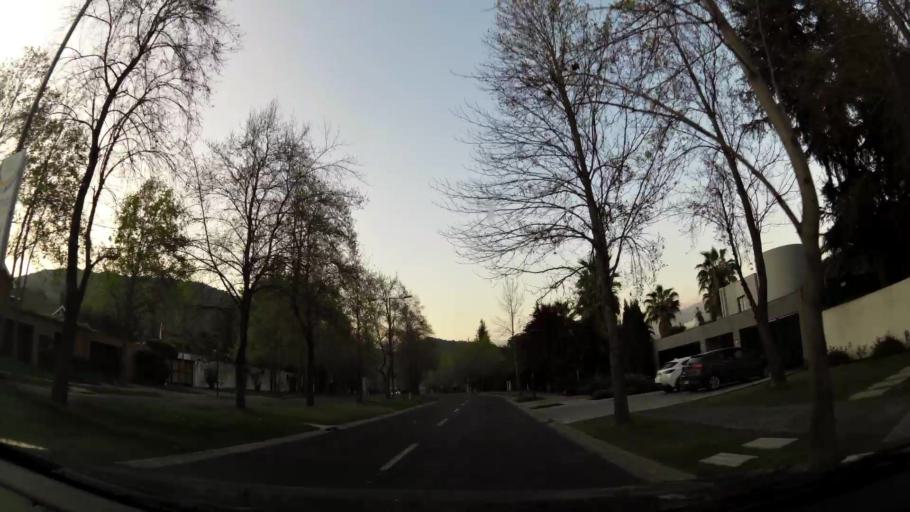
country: CL
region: Santiago Metropolitan
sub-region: Provincia de Chacabuco
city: Chicureo Abajo
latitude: -33.3400
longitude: -70.5539
